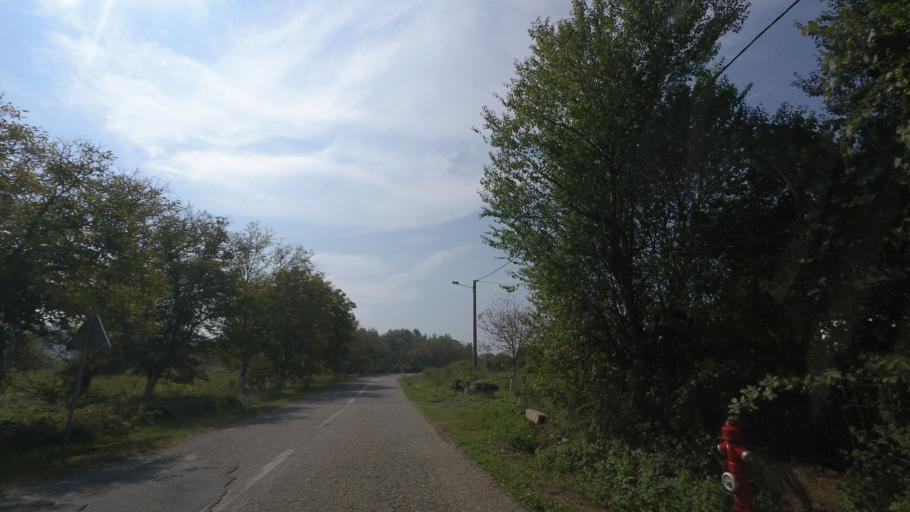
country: BA
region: Republika Srpska
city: Dobrljin
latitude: 45.1629
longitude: 16.4730
